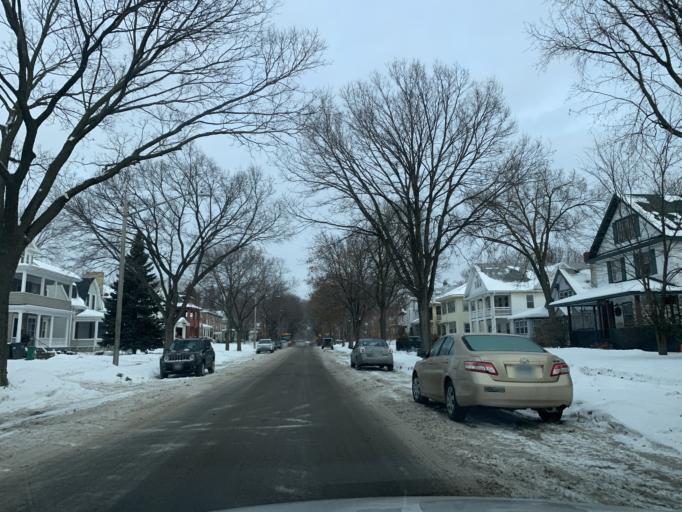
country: US
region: Minnesota
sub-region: Hennepin County
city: Minneapolis
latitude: 44.9560
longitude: -93.2829
